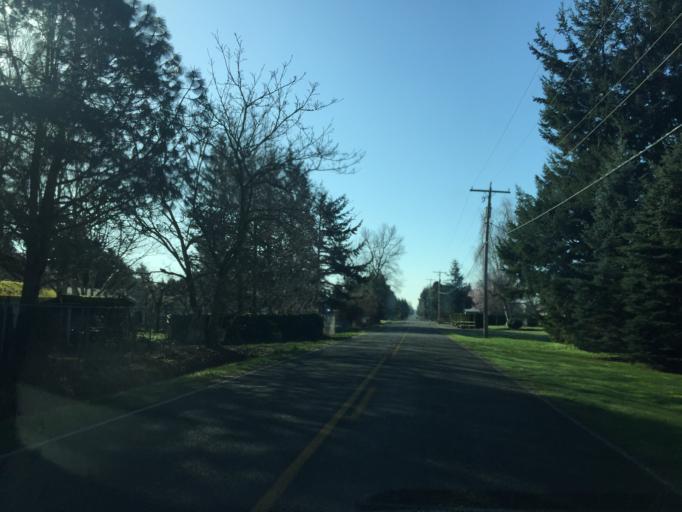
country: US
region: Washington
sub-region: Whatcom County
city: Lynden
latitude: 48.8905
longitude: -122.4968
